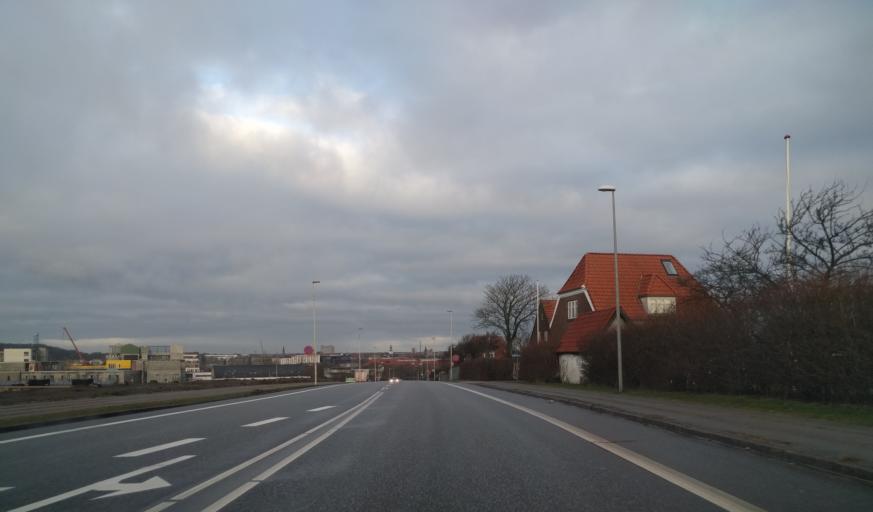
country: DK
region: North Denmark
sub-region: Alborg Kommune
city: Aalborg
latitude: 57.0339
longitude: 9.9417
